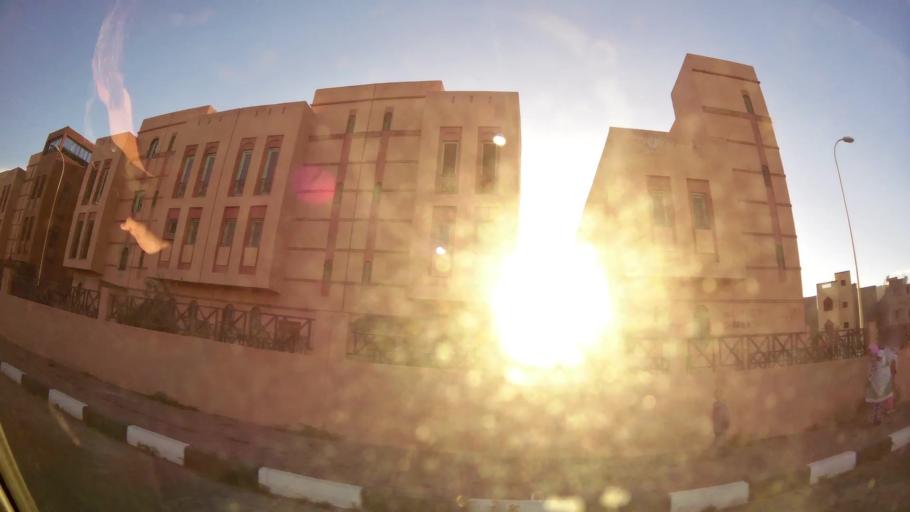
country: MA
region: Marrakech-Tensift-Al Haouz
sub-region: Marrakech
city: Marrakesh
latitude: 31.7445
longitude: -8.1152
